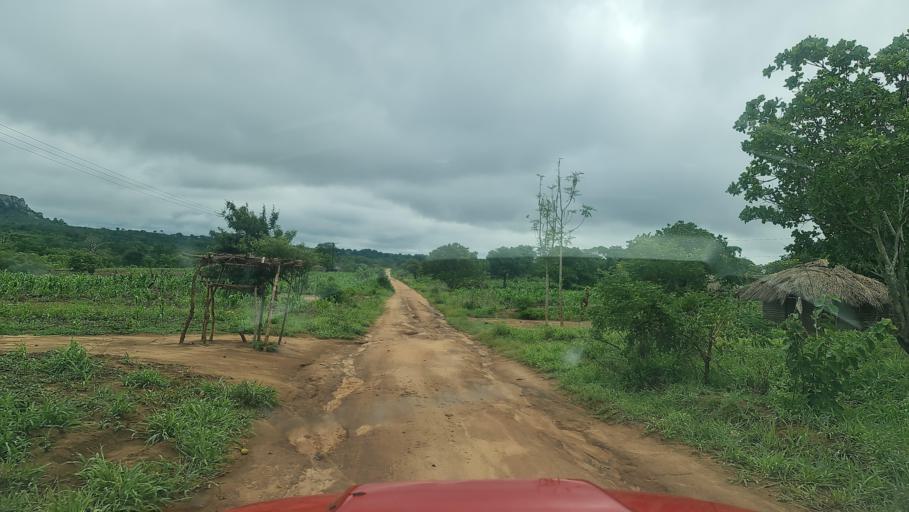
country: MW
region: Southern Region
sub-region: Nsanje District
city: Nsanje
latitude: -17.1917
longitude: 35.8638
